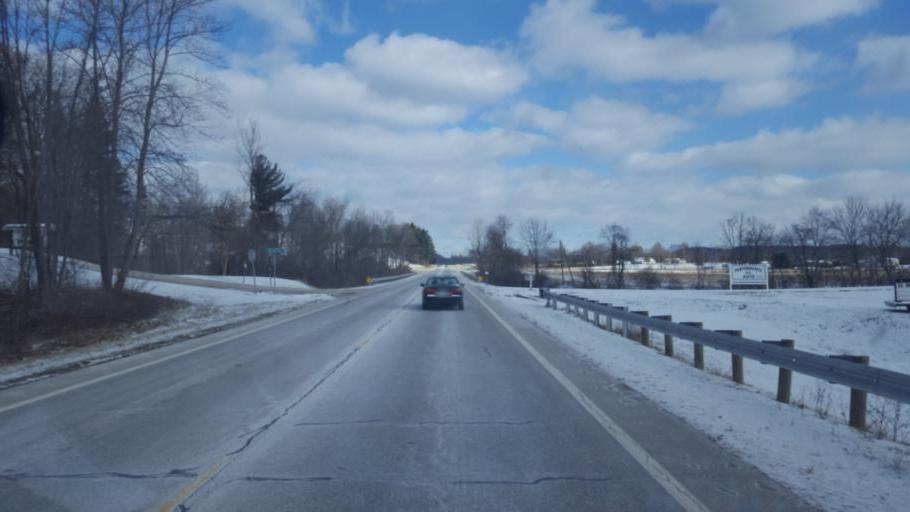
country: US
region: Ohio
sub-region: Coshocton County
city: Coshocton
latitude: 40.1859
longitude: -81.9001
